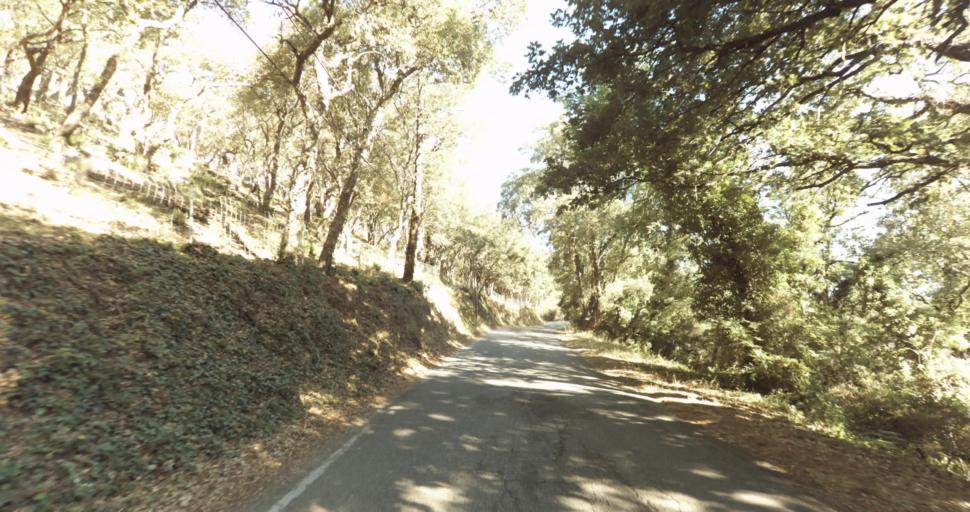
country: FR
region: Provence-Alpes-Cote d'Azur
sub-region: Departement du Var
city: Gassin
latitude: 43.2212
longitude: 6.5921
